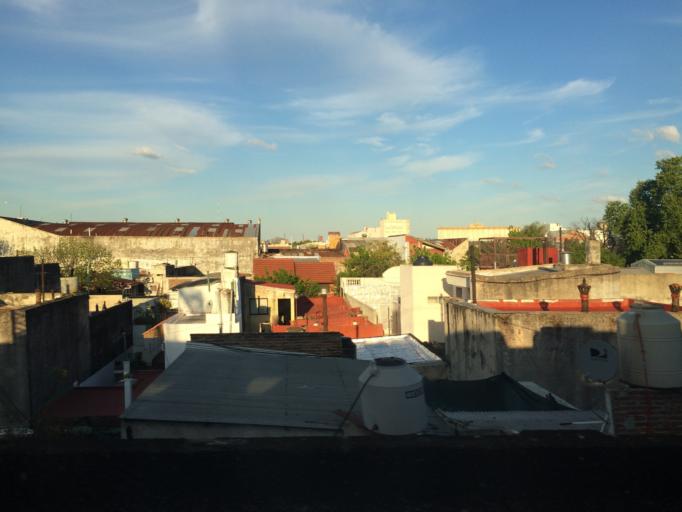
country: AR
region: Buenos Aires
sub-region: Partido de Avellaneda
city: Avellaneda
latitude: -34.6525
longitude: -58.3791
